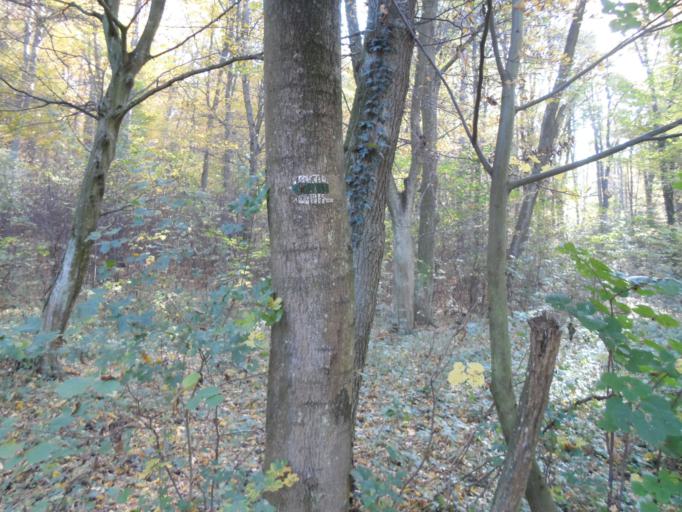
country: HU
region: Veszprem
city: Ajka
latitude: 47.2100
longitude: 17.5623
